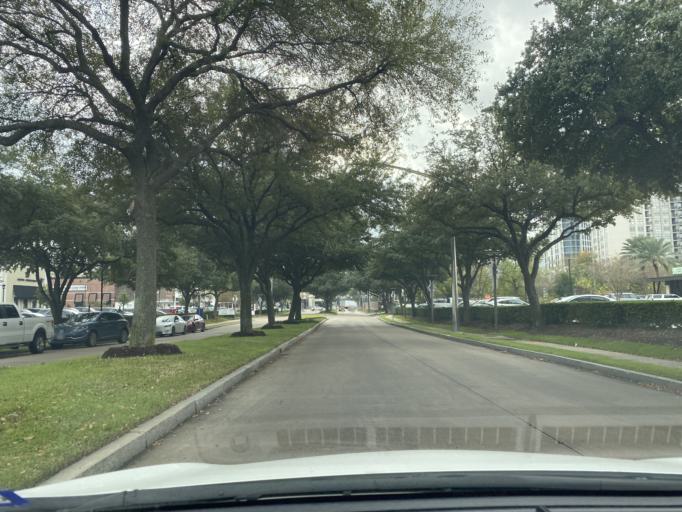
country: US
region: Texas
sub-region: Harris County
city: Hunters Creek Village
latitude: 29.7558
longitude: -95.4578
